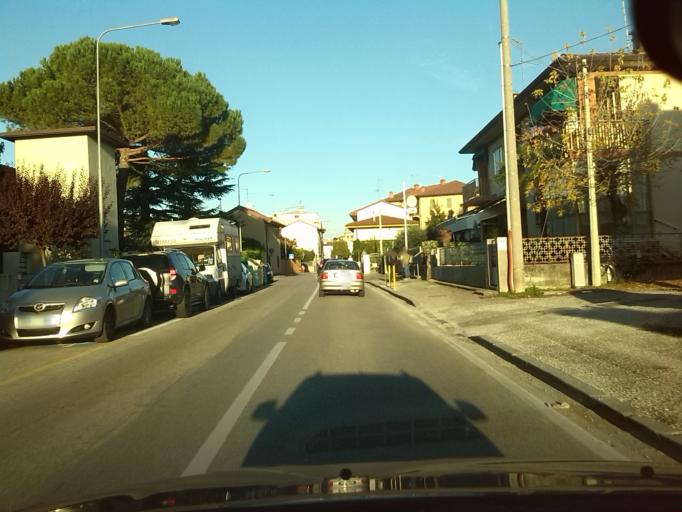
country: IT
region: Friuli Venezia Giulia
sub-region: Provincia di Udine
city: Udine
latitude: 46.0547
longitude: 13.2185
